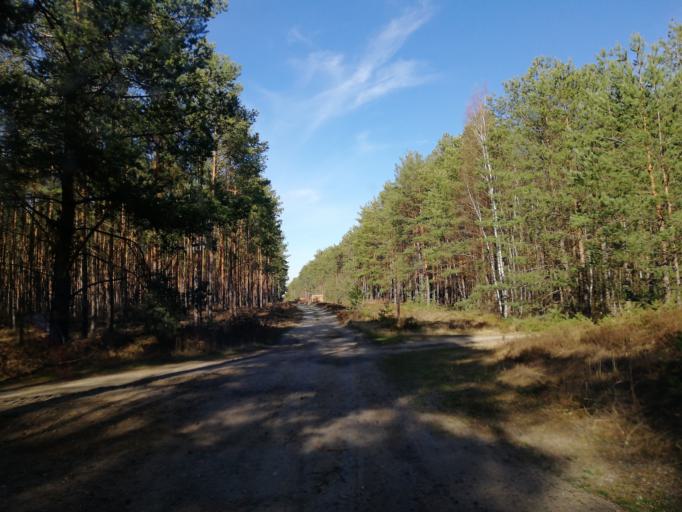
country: DE
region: Brandenburg
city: Ruckersdorf
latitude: 51.5659
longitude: 13.5919
